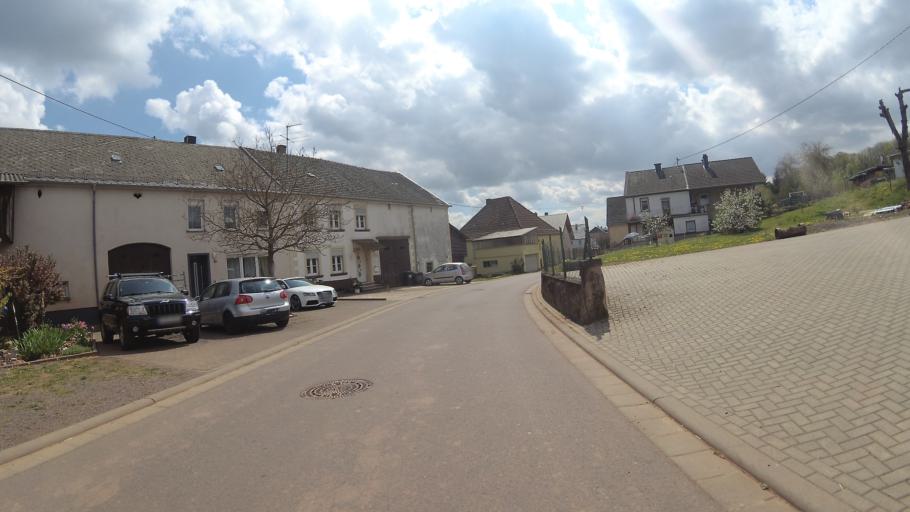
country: DE
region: Saarland
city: Nonnweiler
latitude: 49.5773
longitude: 6.9271
